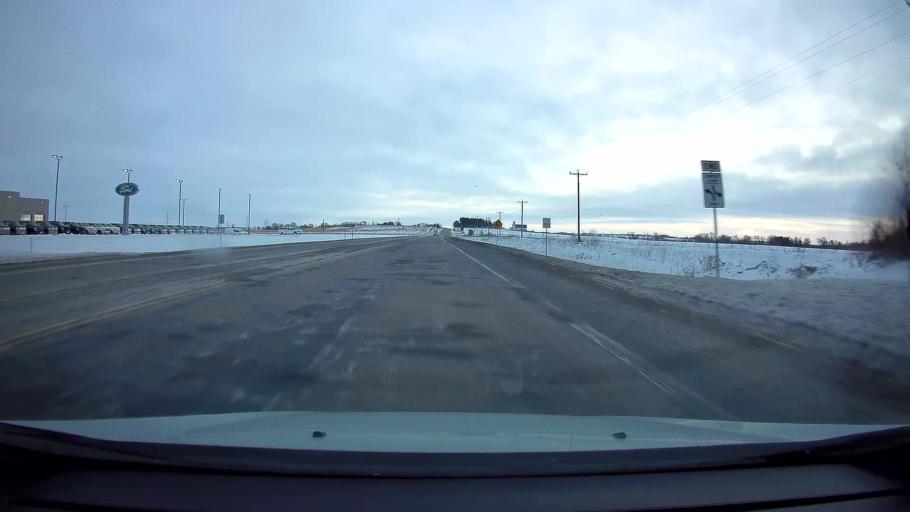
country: US
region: Wisconsin
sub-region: Saint Croix County
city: New Richmond
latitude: 45.1370
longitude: -92.5225
